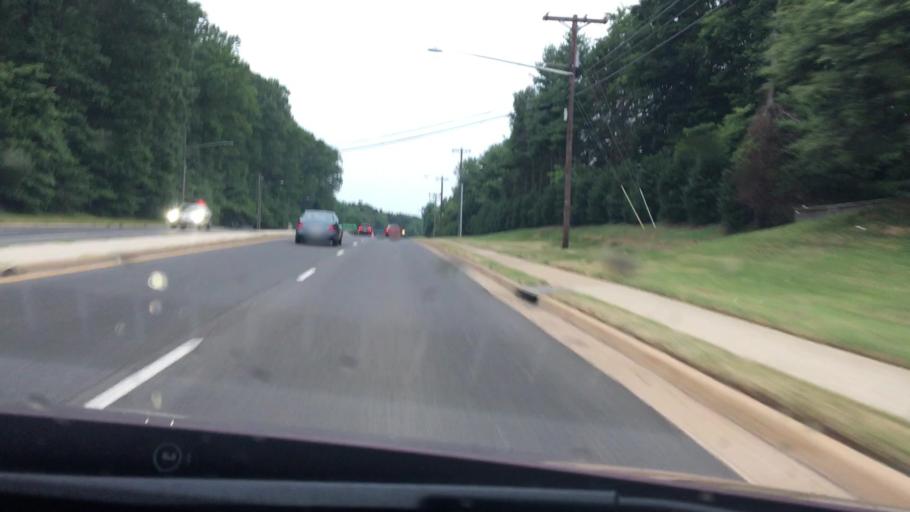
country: US
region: Virginia
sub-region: Fairfax County
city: Centreville
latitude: 38.8274
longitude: -77.3807
